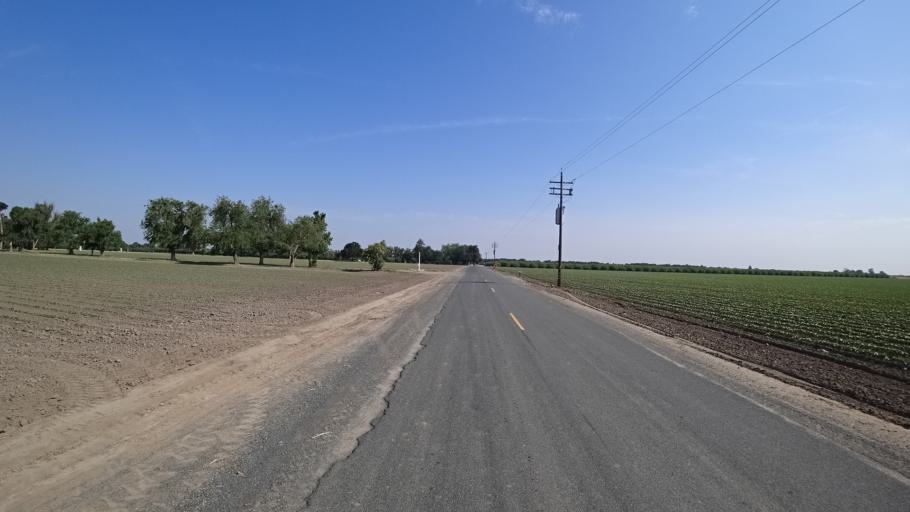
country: US
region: California
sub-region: Kings County
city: Lemoore
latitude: 36.3256
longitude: -119.8438
